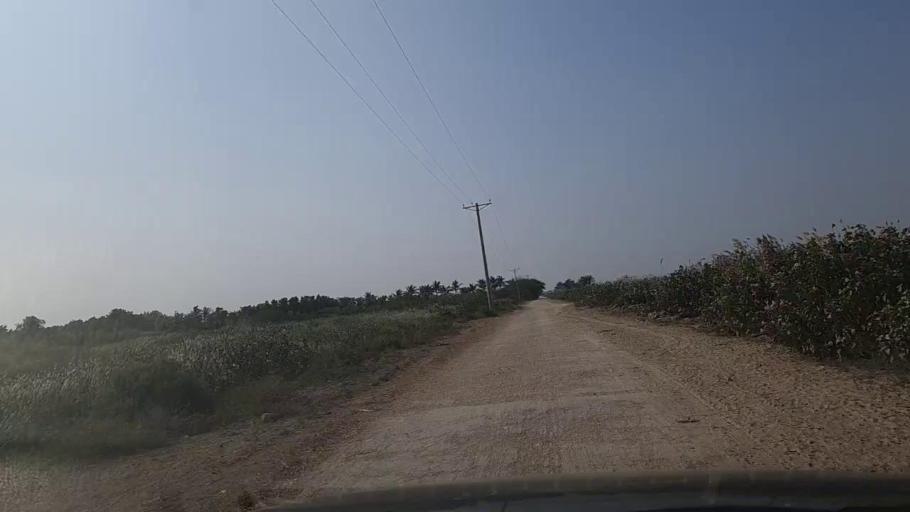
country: PK
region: Sindh
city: Gharo
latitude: 24.6802
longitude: 67.5960
